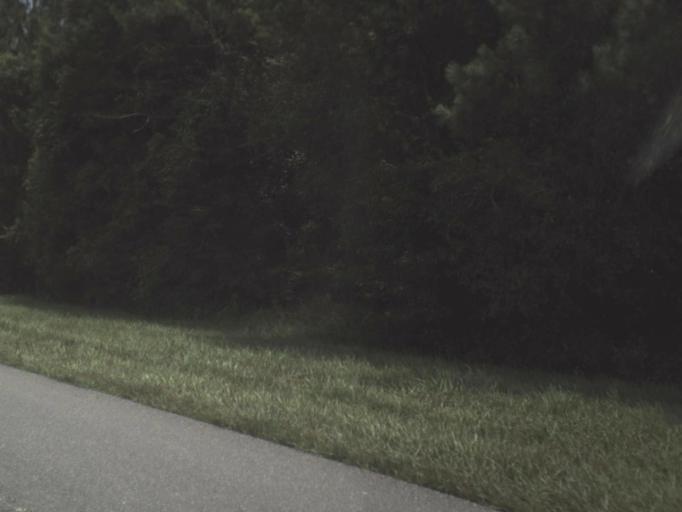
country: US
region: Florida
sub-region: Hernando County
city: Hill 'n Dale
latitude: 28.5137
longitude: -82.2397
